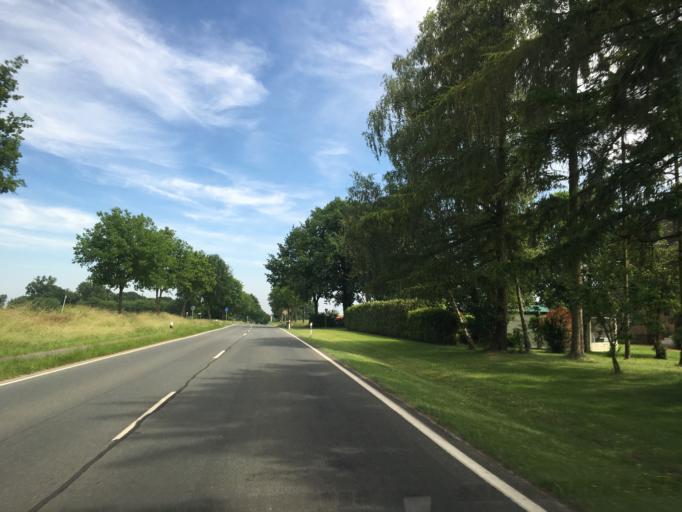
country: DE
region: North Rhine-Westphalia
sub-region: Regierungsbezirk Munster
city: Nordwalde
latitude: 52.0552
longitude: 7.5001
